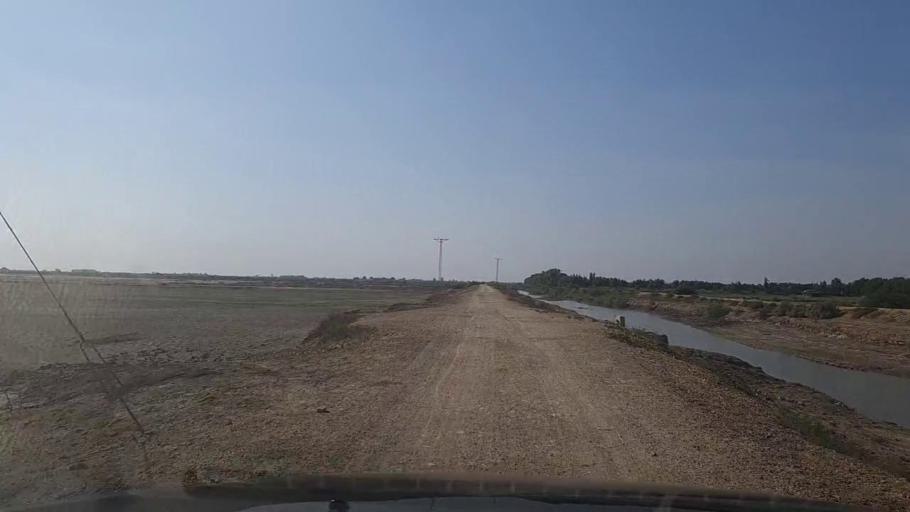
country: PK
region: Sindh
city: Thatta
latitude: 24.7111
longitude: 67.7664
